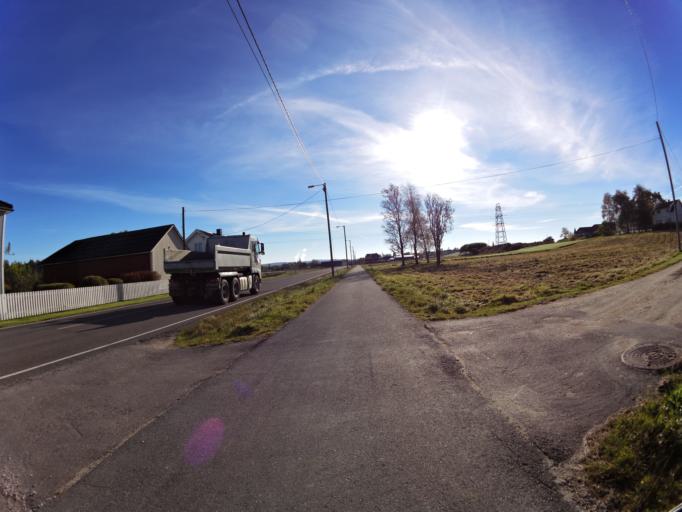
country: NO
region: Ostfold
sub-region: Sarpsborg
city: Sarpsborg
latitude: 59.2768
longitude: 11.0145
